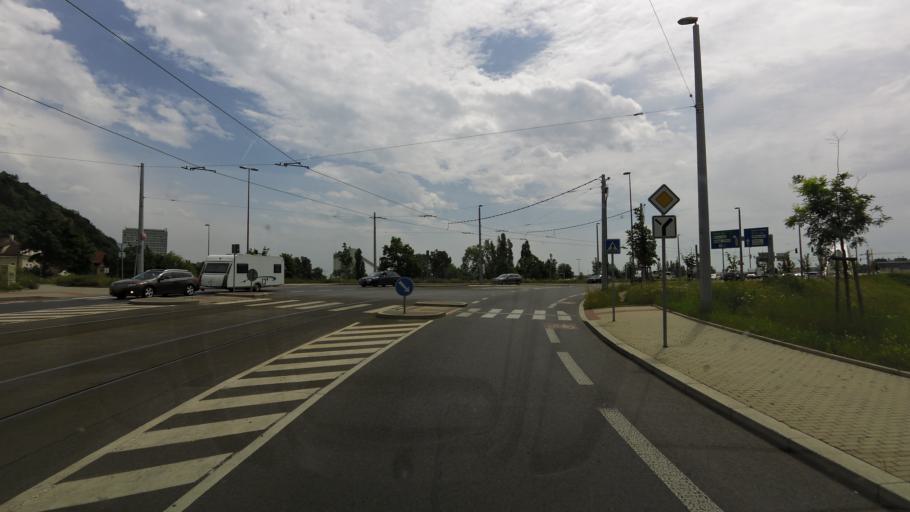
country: CZ
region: Praha
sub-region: Praha 8
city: Karlin
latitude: 50.1159
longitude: 14.4343
